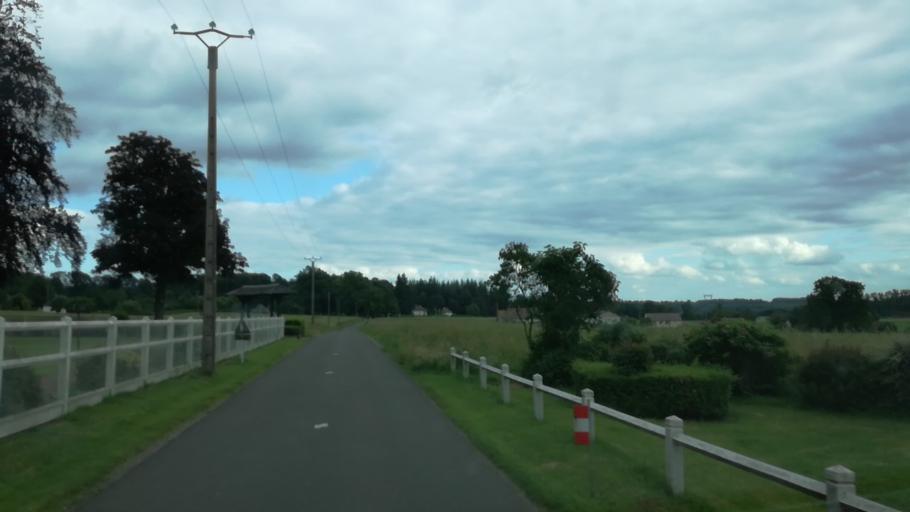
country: FR
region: Haute-Normandie
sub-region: Departement de l'Eure
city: Bourg-Achard
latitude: 49.2926
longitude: 0.8055
